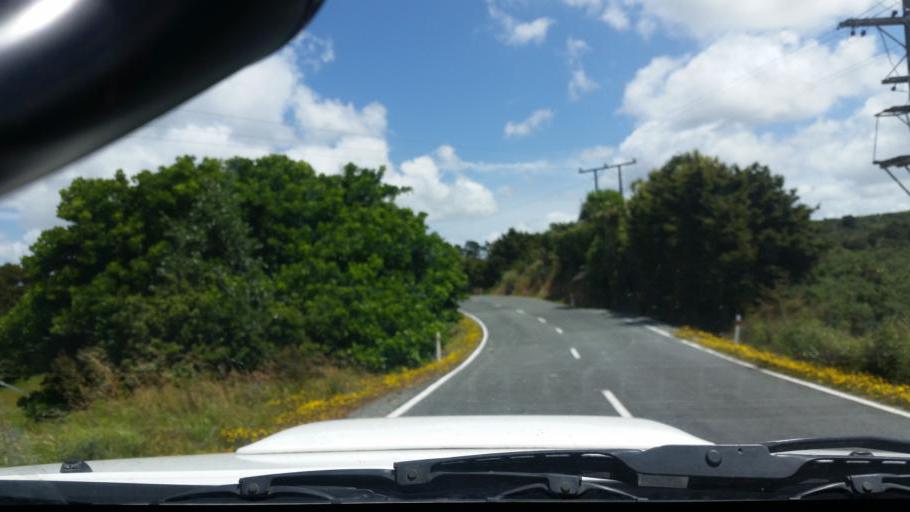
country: NZ
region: Northland
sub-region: Whangarei
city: Ruakaka
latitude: -36.0742
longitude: 174.2601
